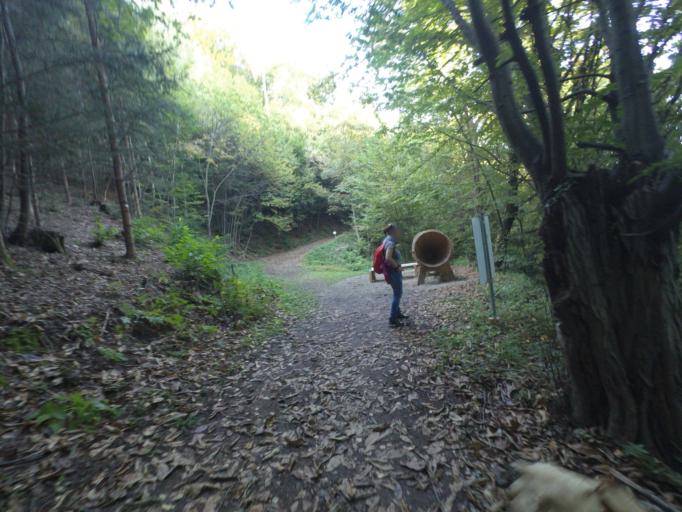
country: AT
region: Styria
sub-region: Politischer Bezirk Leibnitz
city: Kitzeck im Sausal
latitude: 46.7832
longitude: 15.4322
